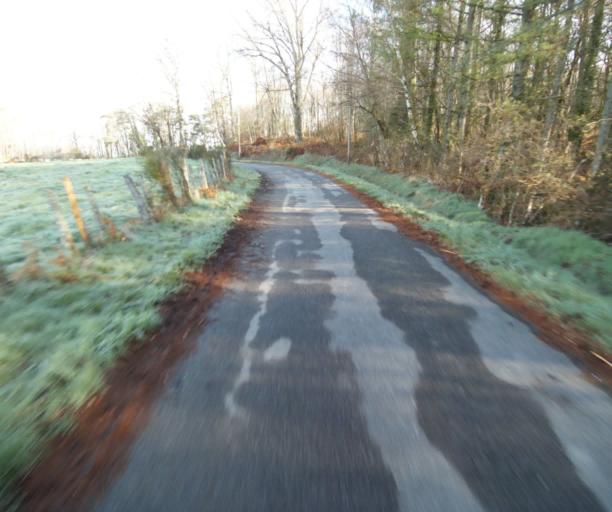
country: FR
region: Limousin
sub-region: Departement de la Correze
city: Correze
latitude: 45.2886
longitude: 1.8638
